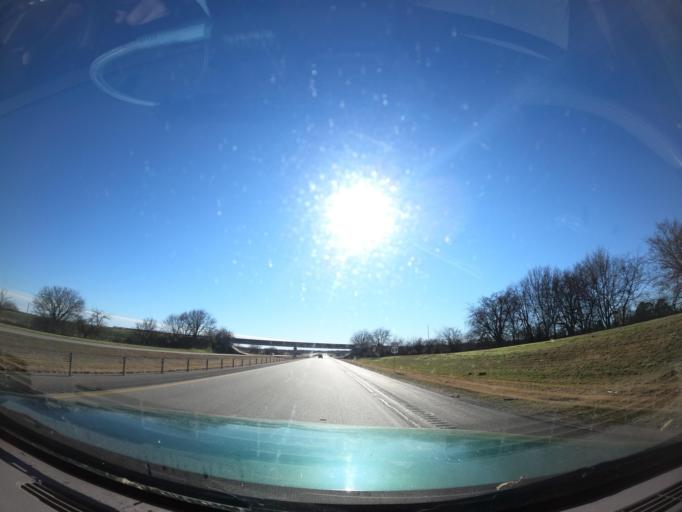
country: US
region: Oklahoma
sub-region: McIntosh County
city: Checotah
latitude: 35.4507
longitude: -95.5478
